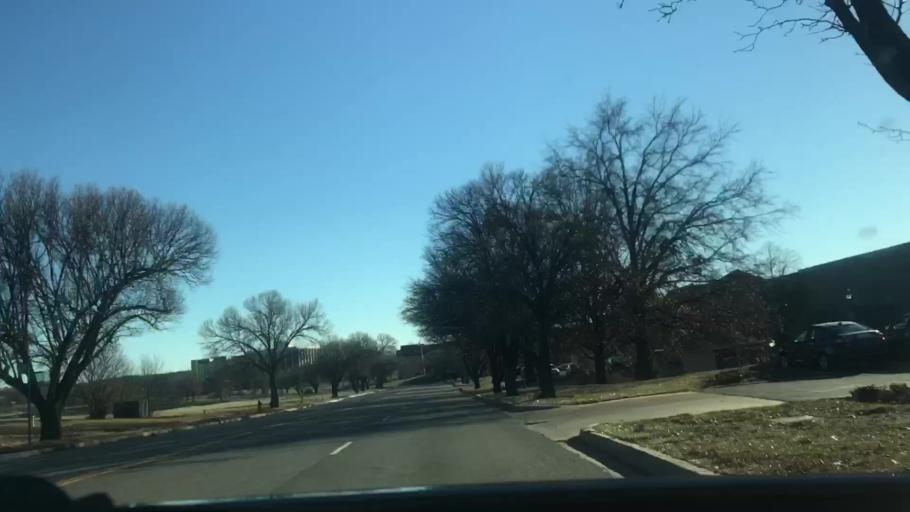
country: US
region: Missouri
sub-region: Platte County
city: Weatherby Lake
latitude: 39.2956
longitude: -94.6818
